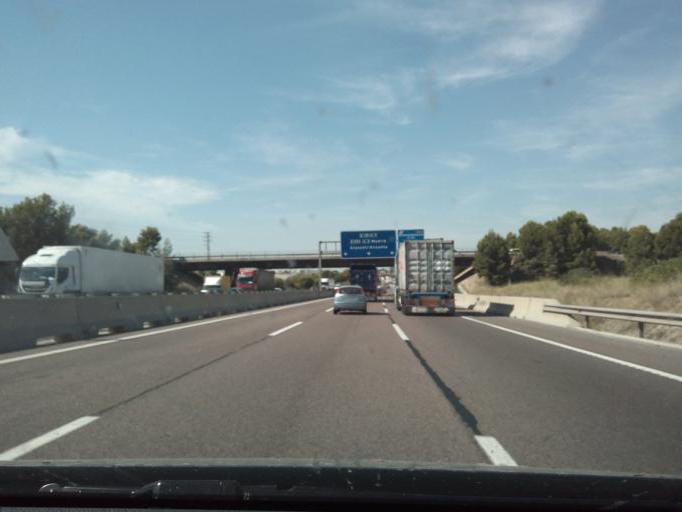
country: ES
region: Valencia
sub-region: Provincia de Valencia
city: Manises
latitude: 39.5273
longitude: -0.4666
